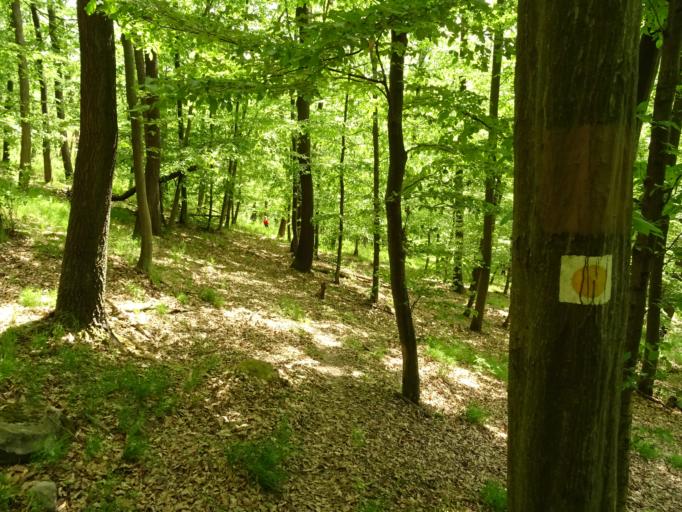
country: SK
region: Nitriansky
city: Sahy
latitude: 47.9938
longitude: 18.9523
